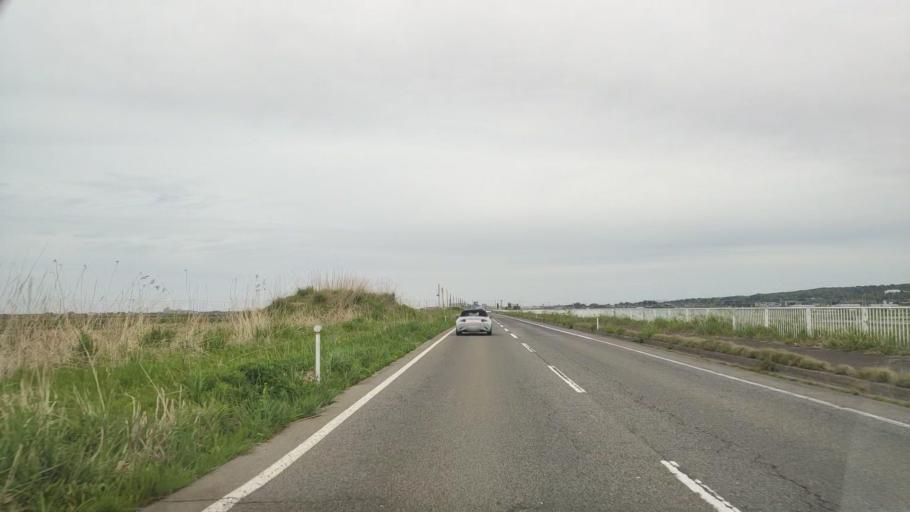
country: JP
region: Niigata
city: Niitsu-honcho
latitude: 37.7649
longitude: 139.0981
